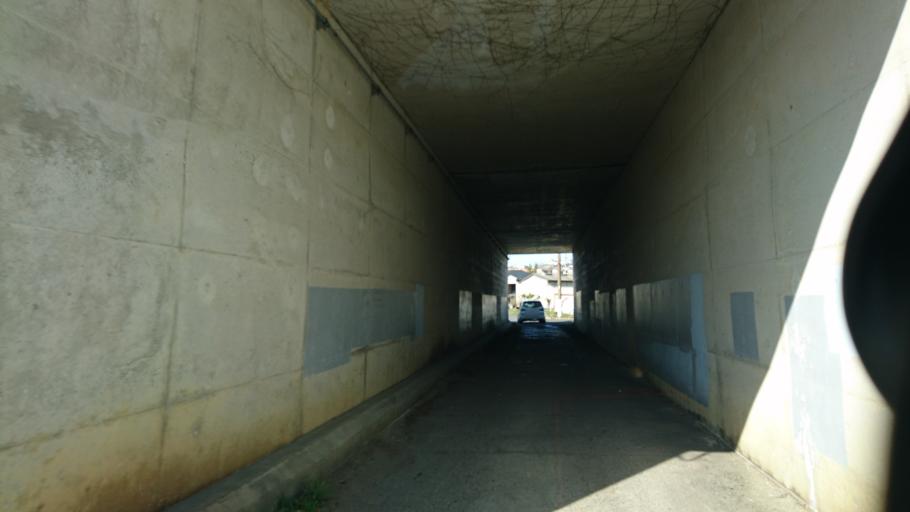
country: JP
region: Gifu
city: Nakatsugawa
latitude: 35.4605
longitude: 137.4102
